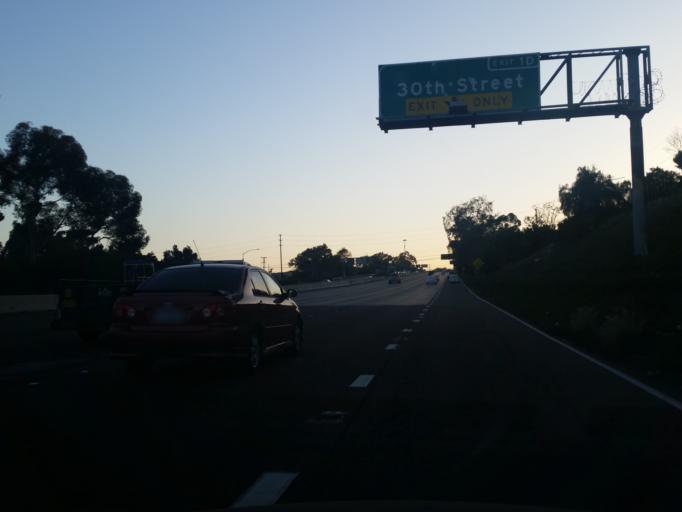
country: US
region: California
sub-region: San Diego County
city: San Diego
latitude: 32.7166
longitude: -117.1208
